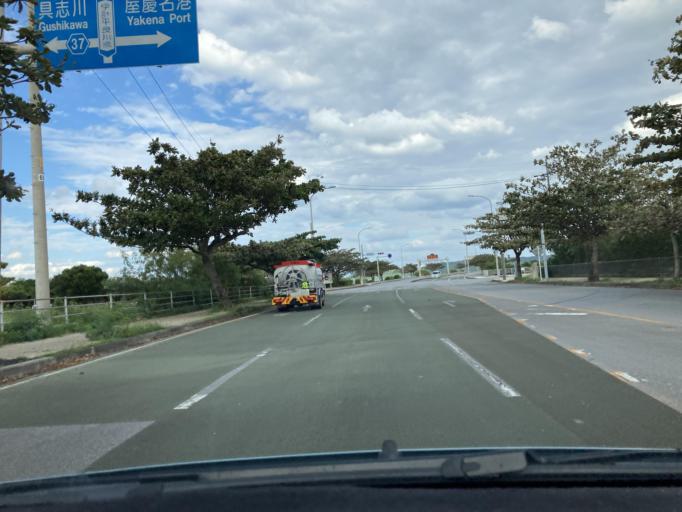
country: JP
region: Okinawa
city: Katsuren-haebaru
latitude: 26.3306
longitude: 127.9047
